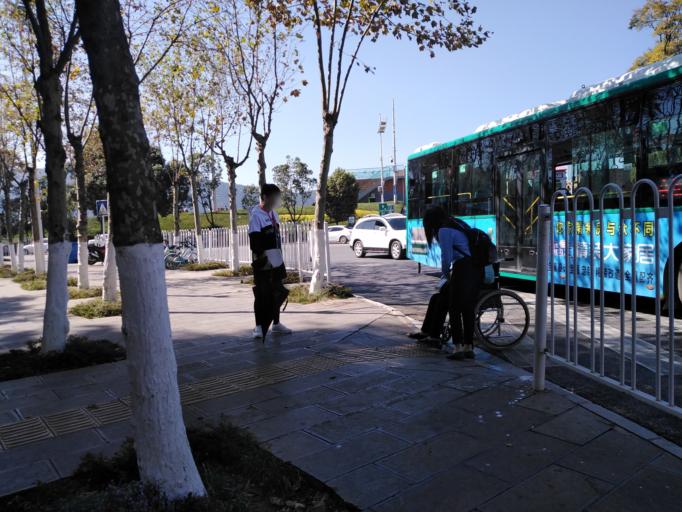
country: CN
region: Yunnan
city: Gaoyao
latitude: 24.9865
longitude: 102.6497
